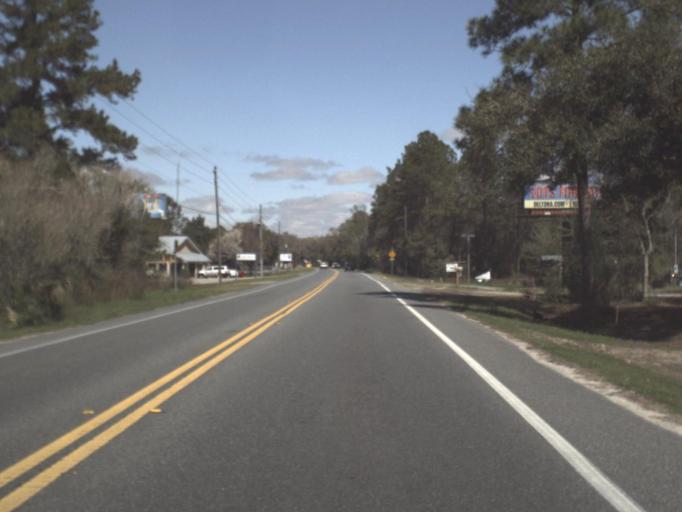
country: US
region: Florida
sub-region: Wakulla County
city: Crawfordville
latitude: 30.0872
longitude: -84.3866
